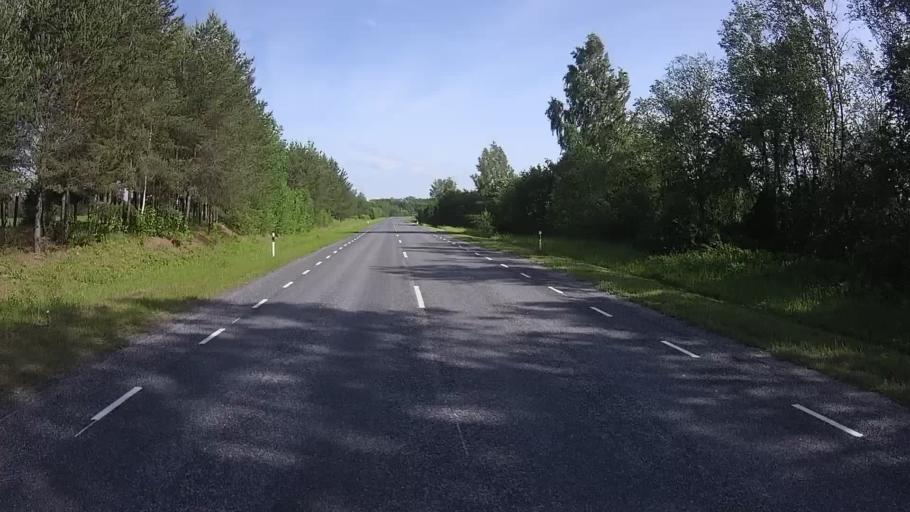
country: EE
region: Valgamaa
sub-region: Torva linn
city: Torva
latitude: 58.0354
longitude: 25.9711
